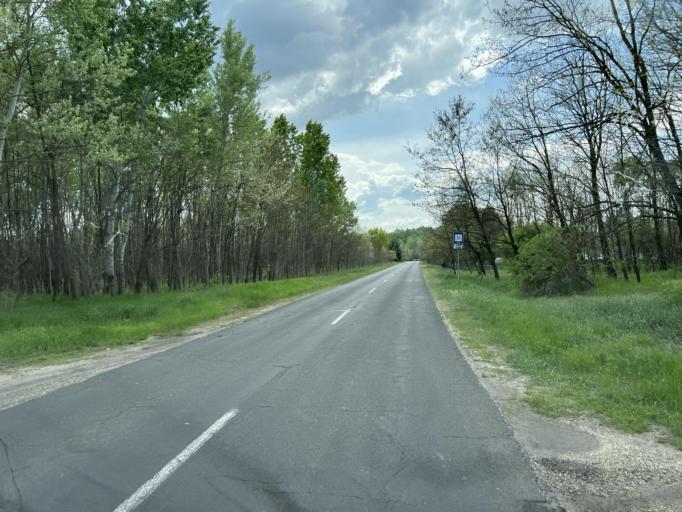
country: HU
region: Pest
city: Csemo
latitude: 47.1014
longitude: 19.6371
